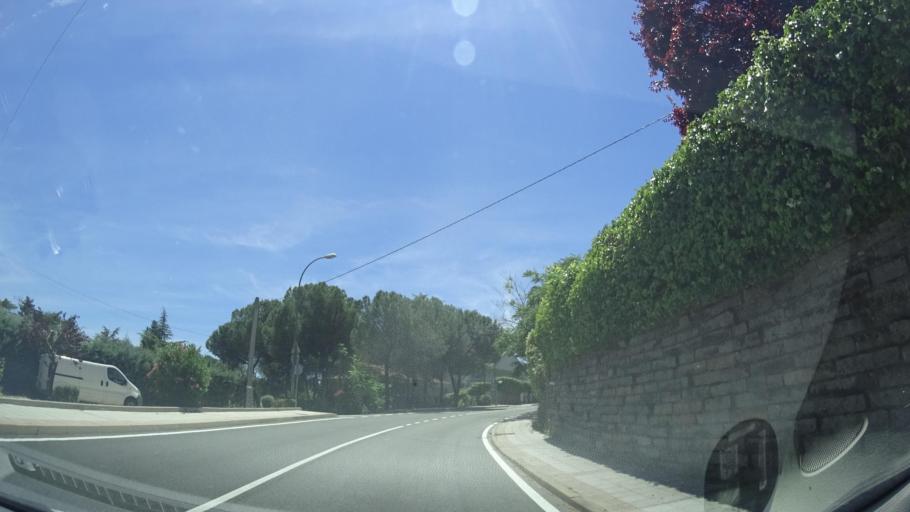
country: ES
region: Madrid
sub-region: Provincia de Madrid
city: Galapagar
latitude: 40.5937
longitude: -3.9870
